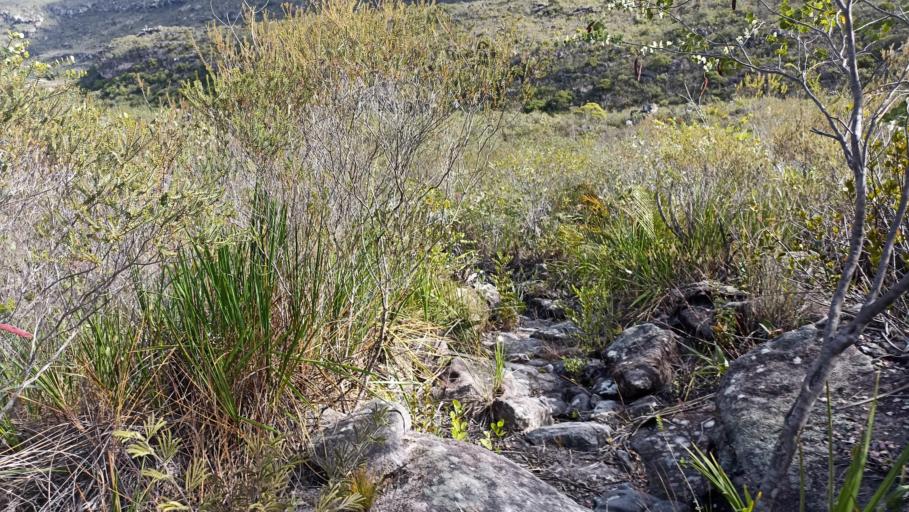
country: BR
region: Bahia
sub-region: Andarai
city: Vera Cruz
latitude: -12.9983
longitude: -41.3764
